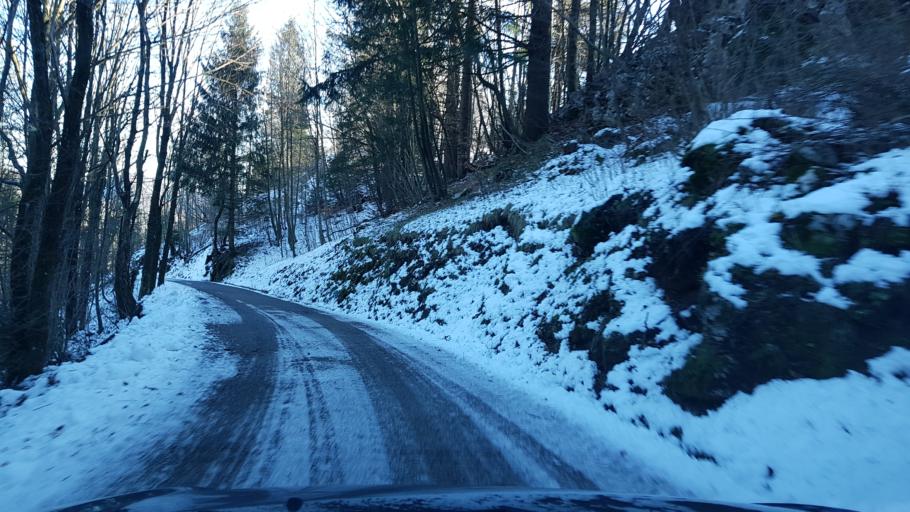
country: IT
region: Friuli Venezia Giulia
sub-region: Provincia di Udine
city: Savogna
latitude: 46.1913
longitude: 13.5277
